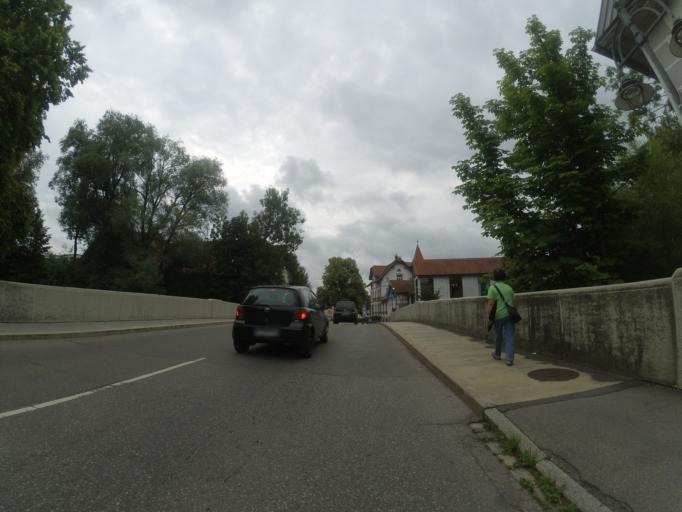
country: DE
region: Baden-Wuerttemberg
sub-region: Tuebingen Region
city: Wangen im Allgau
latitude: 47.6844
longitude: 9.8358
